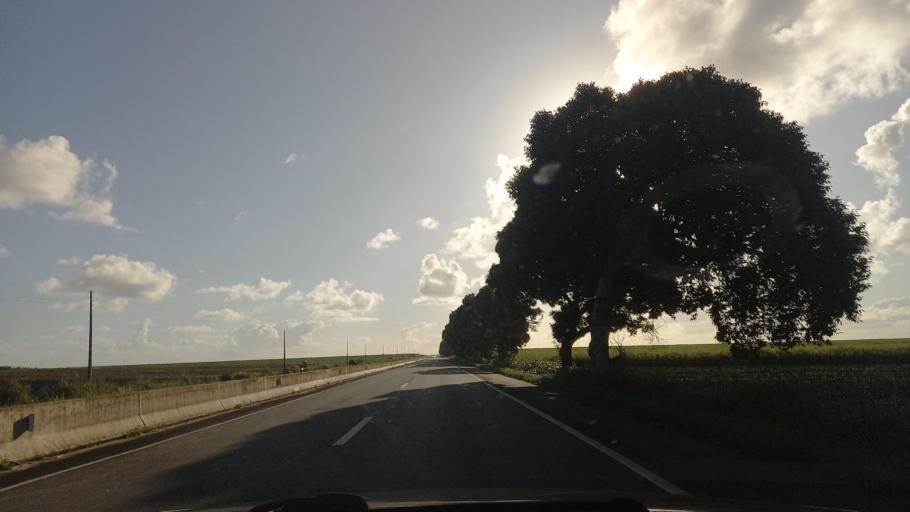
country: BR
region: Alagoas
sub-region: Sao Miguel Dos Campos
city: Sao Miguel dos Campos
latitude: -9.8020
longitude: -36.1495
